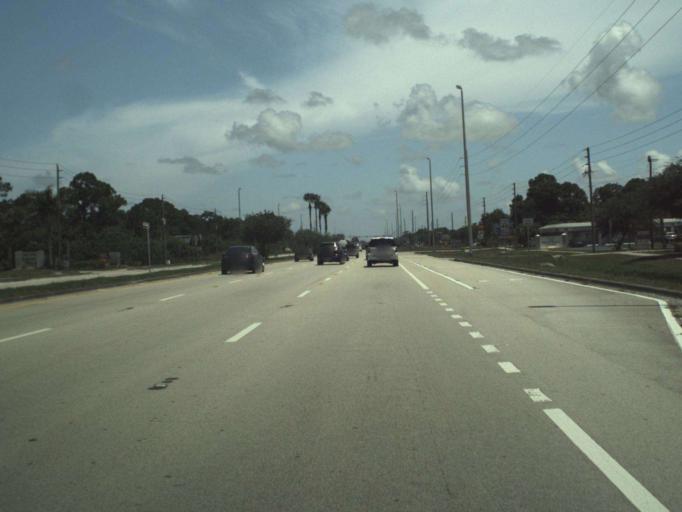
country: US
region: Florida
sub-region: Saint Lucie County
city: River Park
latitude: 27.3157
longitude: -80.3145
